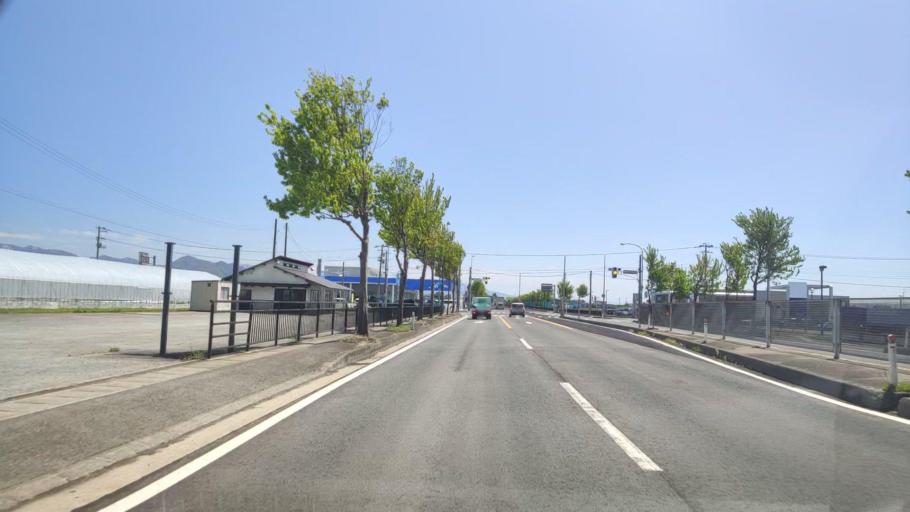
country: JP
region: Yamagata
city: Higashine
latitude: 38.4593
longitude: 140.3825
